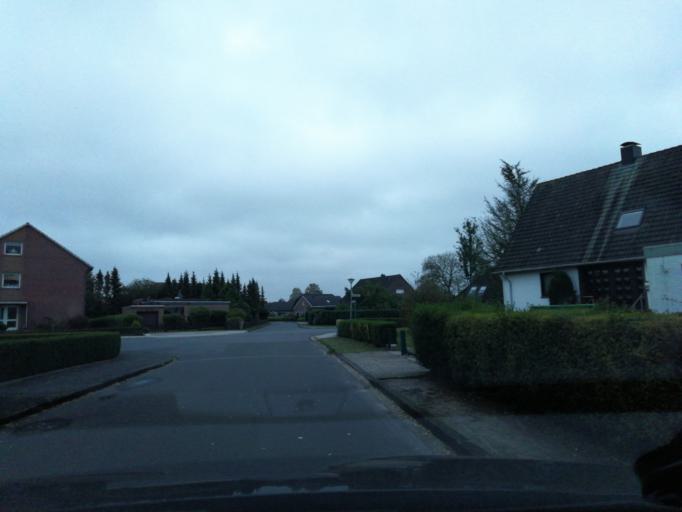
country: DE
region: Lower Saxony
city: Schortens
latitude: 53.5433
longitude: 7.9317
